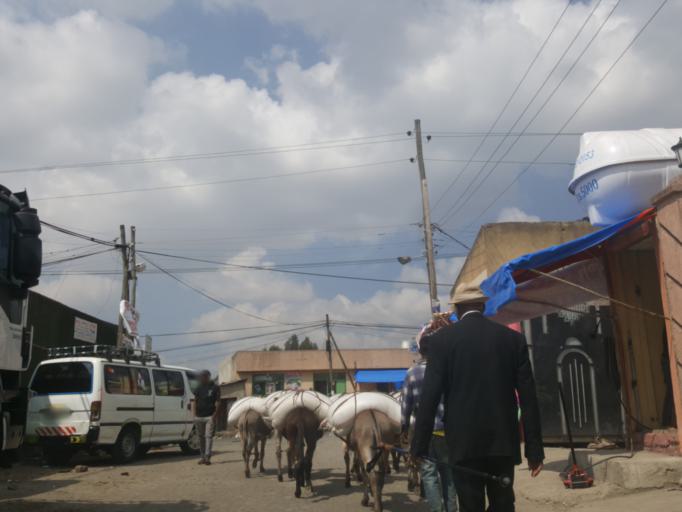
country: ET
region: Adis Abeba
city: Addis Ababa
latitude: 9.0615
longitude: 38.7200
